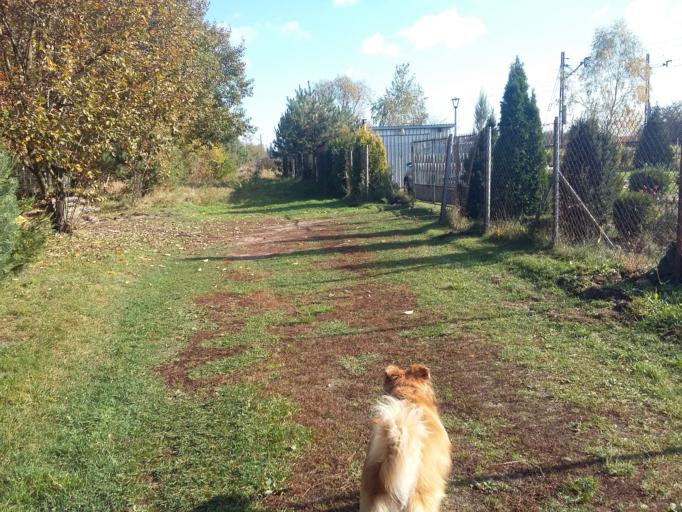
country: PL
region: Lodz Voivodeship
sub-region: Powiat pabianicki
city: Ksawerow
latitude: 51.7338
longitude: 19.3826
